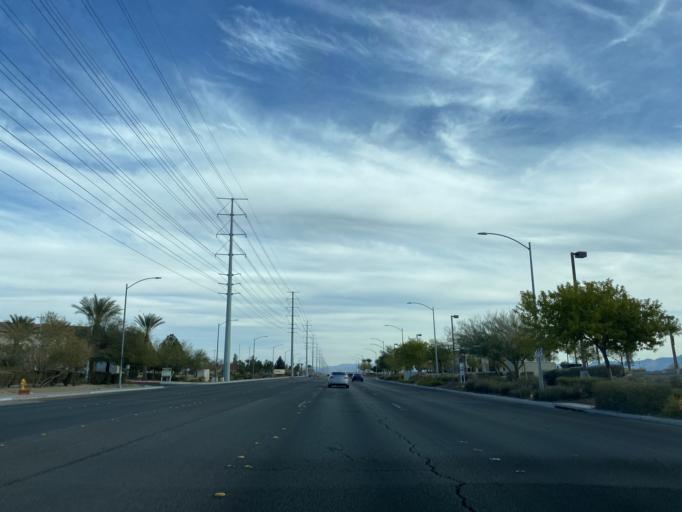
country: US
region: Nevada
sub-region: Clark County
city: Enterprise
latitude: 36.0555
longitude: -115.2746
